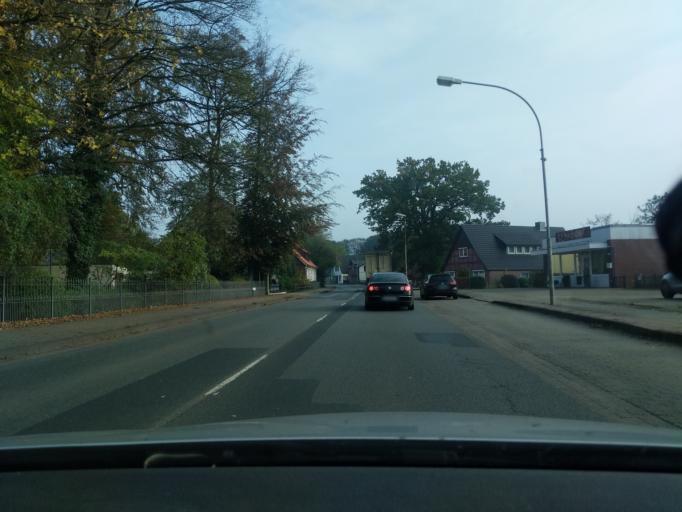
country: DE
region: Lower Saxony
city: Himmelpforten
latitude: 53.6137
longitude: 9.3065
